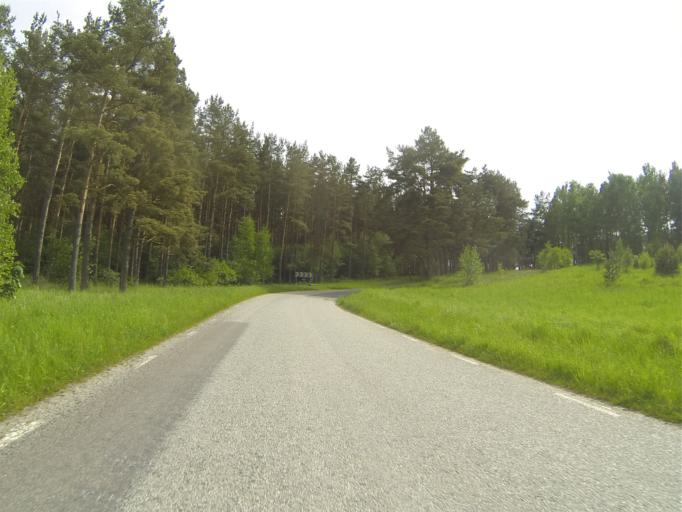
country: SE
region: Skane
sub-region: Sjobo Kommun
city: Blentarp
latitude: 55.6607
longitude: 13.6150
